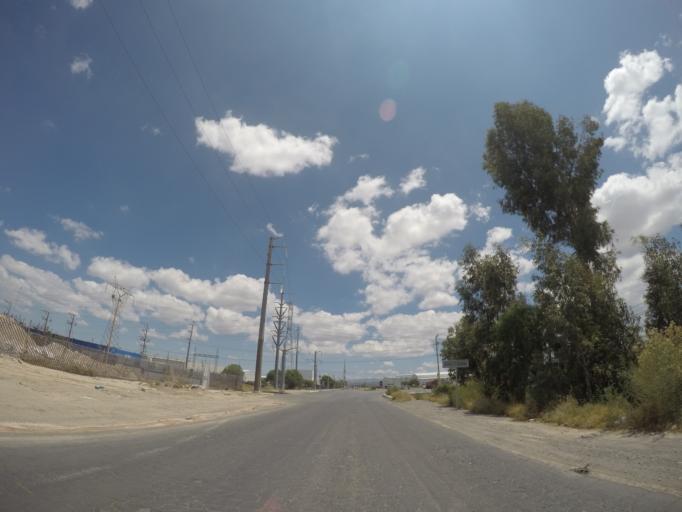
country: MX
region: San Luis Potosi
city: La Pila
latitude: 22.0489
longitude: -100.8706
